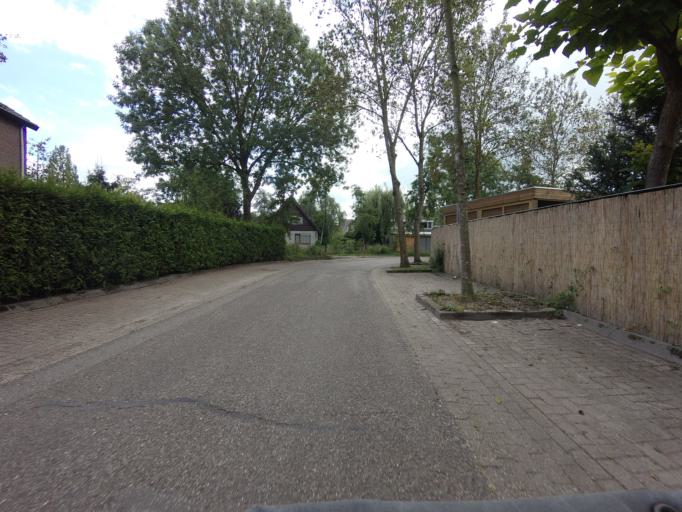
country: NL
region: Utrecht
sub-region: Gemeente IJsselstein
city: IJsselstein
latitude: 52.0187
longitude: 5.0346
